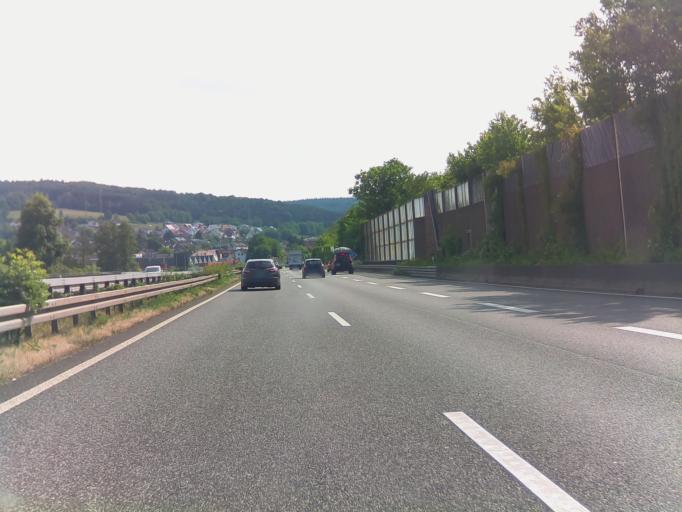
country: DE
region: Hesse
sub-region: Regierungsbezirk Darmstadt
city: Bad Soden-Salmunster
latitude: 50.2759
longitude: 9.3742
